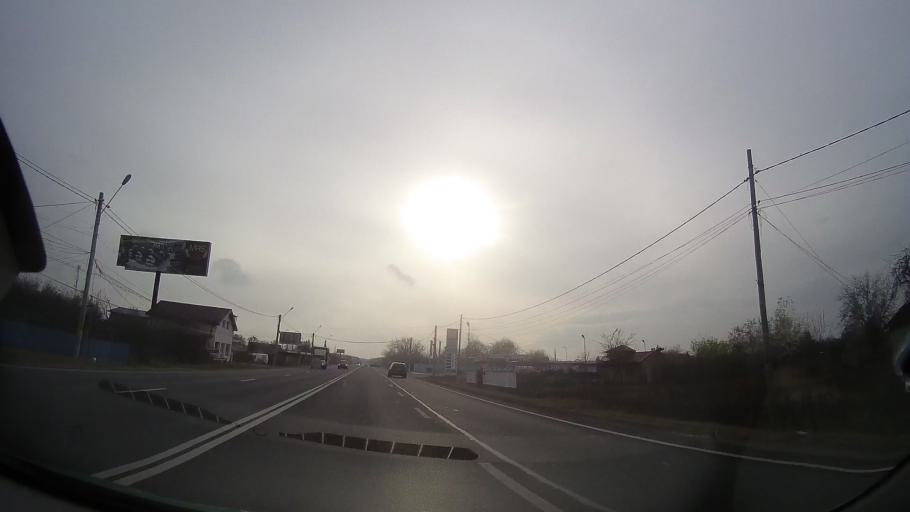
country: RO
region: Ilfov
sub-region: Comuna Ciolpani
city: Ciolpani
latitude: 44.7190
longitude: 26.1031
